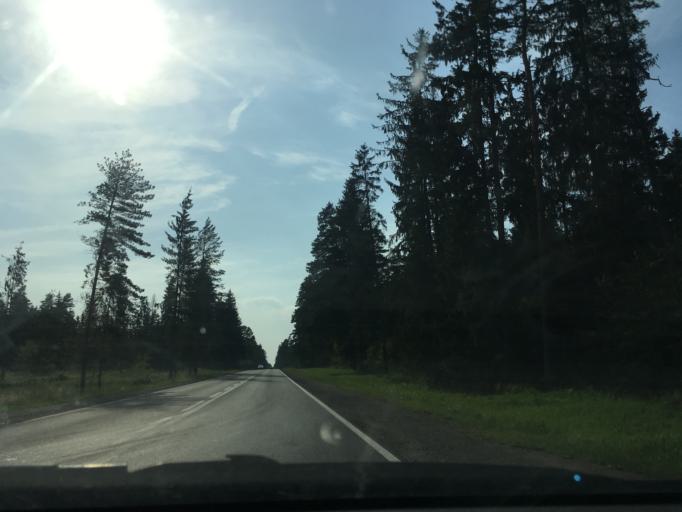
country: PL
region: Podlasie
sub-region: Powiat bialostocki
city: Suprasl
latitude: 53.1256
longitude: 23.3590
